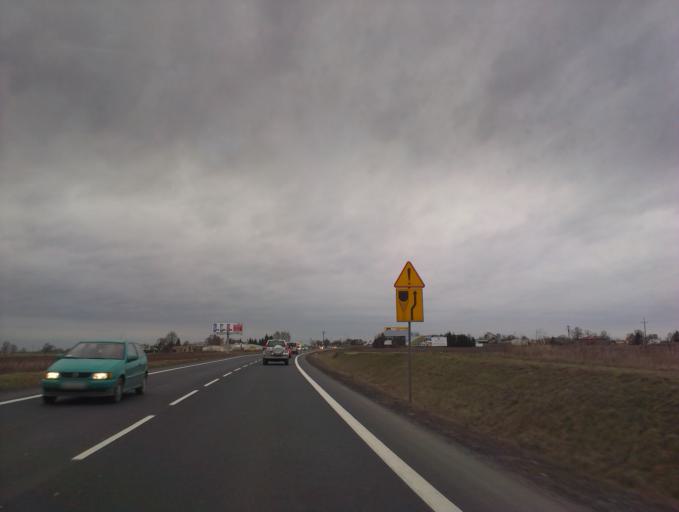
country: PL
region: Greater Poland Voivodeship
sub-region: Powiat poznanski
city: Zlotniki
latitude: 52.5555
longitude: 16.8350
